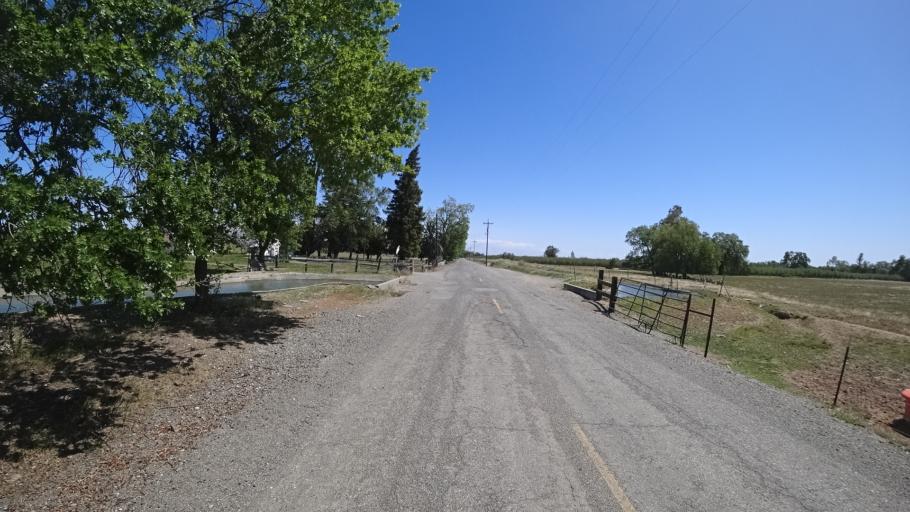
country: US
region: California
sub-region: Glenn County
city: Orland
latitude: 39.7952
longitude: -122.2415
